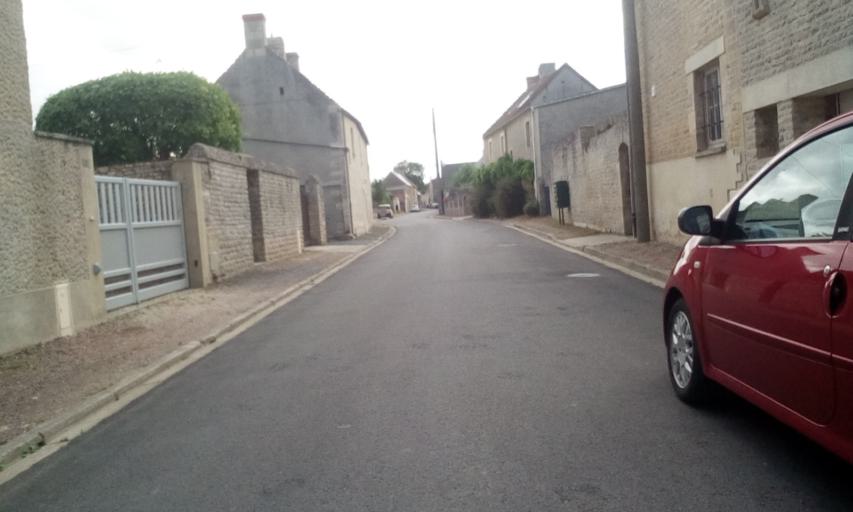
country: FR
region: Lower Normandy
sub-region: Departement du Calvados
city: Courseulles-sur-Mer
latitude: 49.3091
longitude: -0.4919
